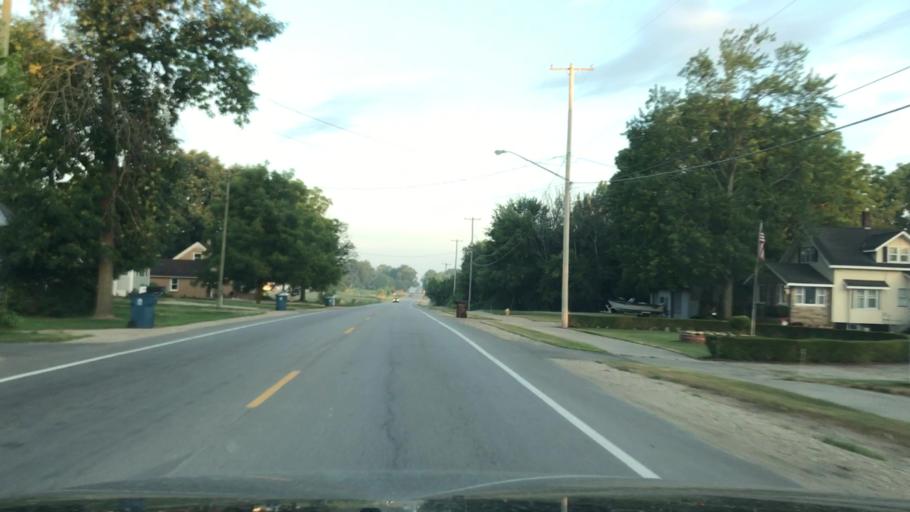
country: US
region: Michigan
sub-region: Ottawa County
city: Zeeland
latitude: 42.7829
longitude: -85.9410
